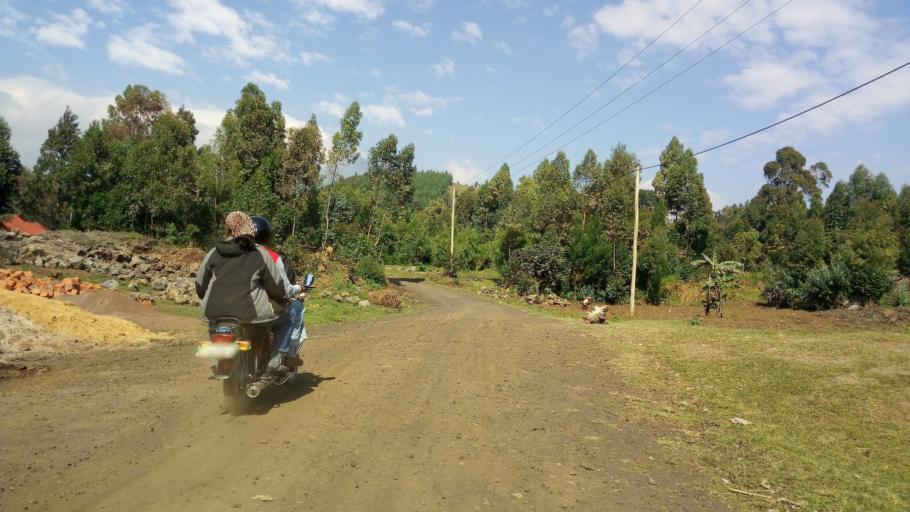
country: UG
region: Western Region
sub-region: Kisoro District
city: Kisoro
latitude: -1.3369
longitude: 29.6348
